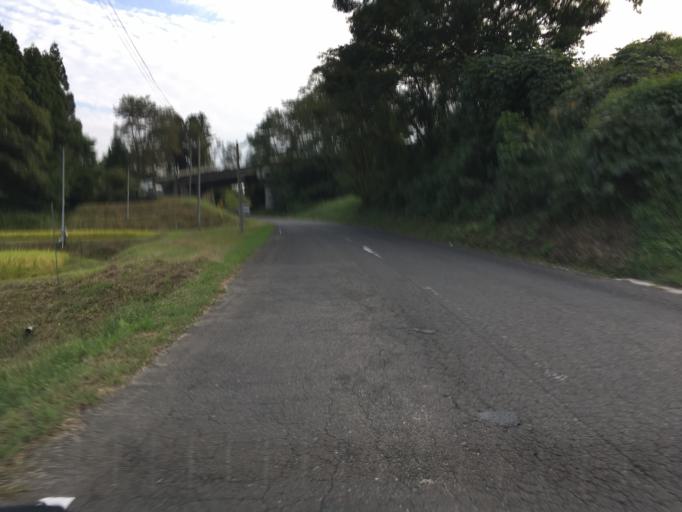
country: JP
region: Fukushima
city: Fukushima-shi
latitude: 37.6872
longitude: 140.5490
